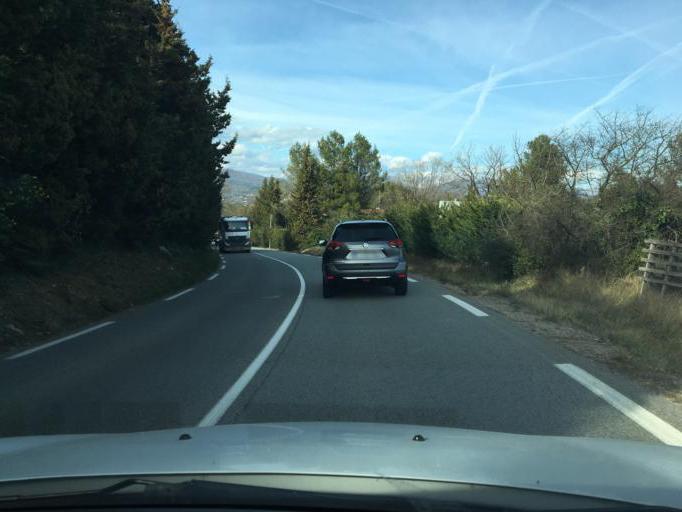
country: FR
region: Provence-Alpes-Cote d'Azur
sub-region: Departement du Var
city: Saint-Paul-en-Foret
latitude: 43.5945
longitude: 6.6892
